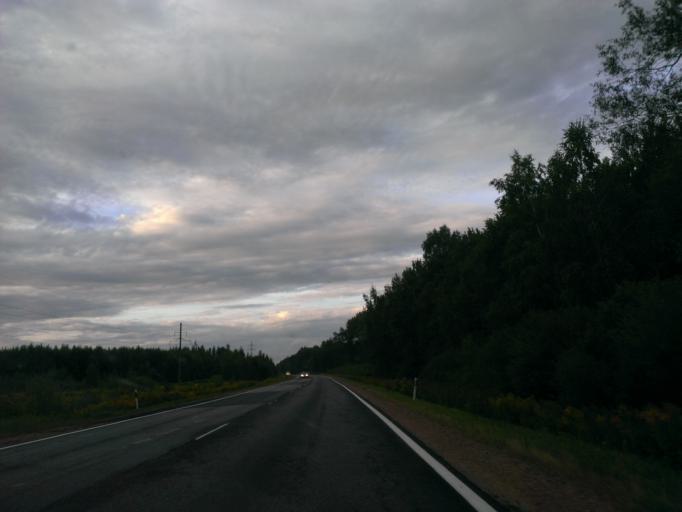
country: LV
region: Salaspils
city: Salaspils
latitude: 56.8645
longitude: 24.4062
